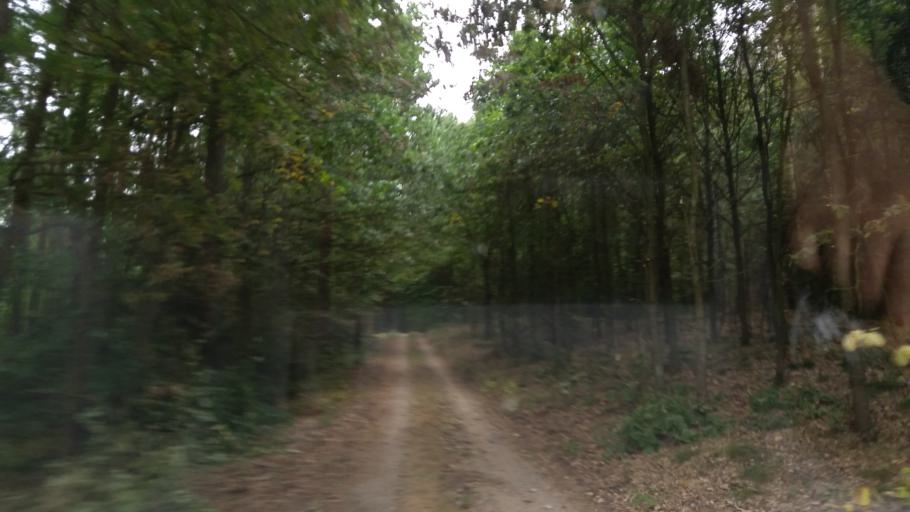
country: PL
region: West Pomeranian Voivodeship
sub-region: Powiat choszczenski
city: Bierzwnik
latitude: 52.9786
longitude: 15.6150
